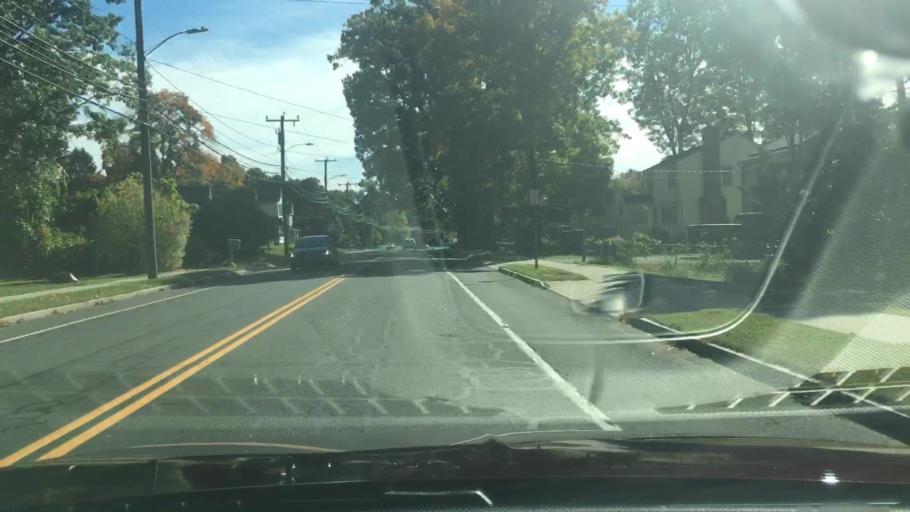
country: US
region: Connecticut
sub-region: Hartford County
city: Manchester
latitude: 41.8050
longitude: -72.5182
